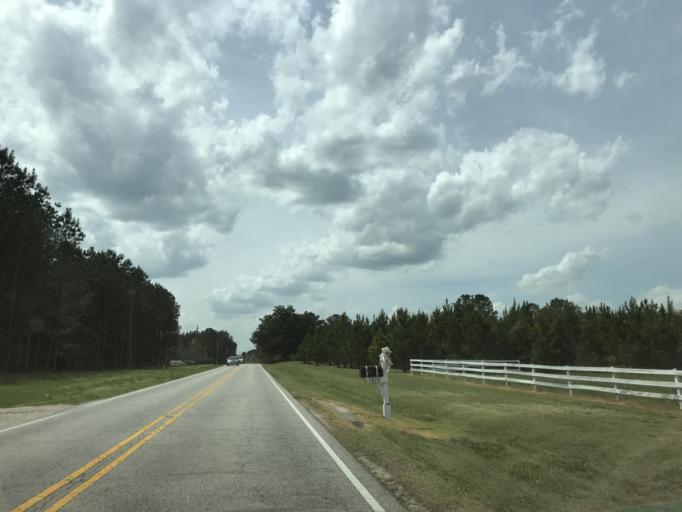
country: US
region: North Carolina
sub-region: Nash County
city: Spring Hope
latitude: 35.9661
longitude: -78.2266
